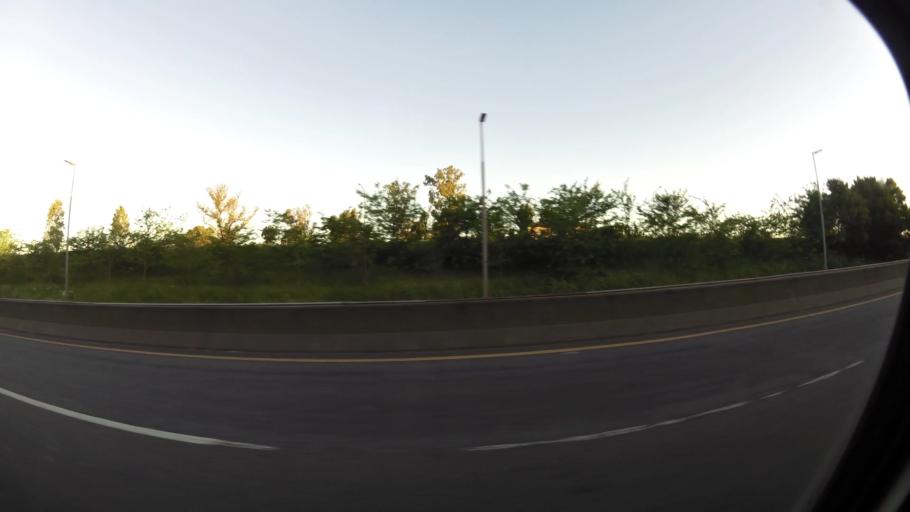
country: AR
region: Buenos Aires
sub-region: Partido de Quilmes
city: Quilmes
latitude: -34.8192
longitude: -58.1864
